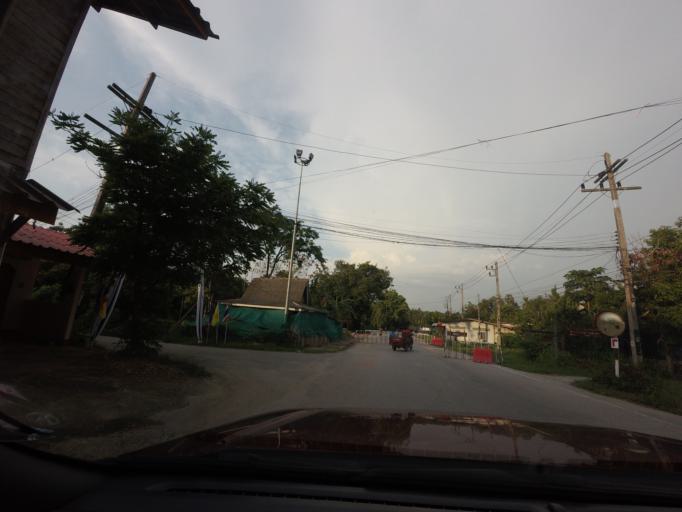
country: TH
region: Pattani
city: Khok Pho
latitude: 6.6742
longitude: 101.1121
